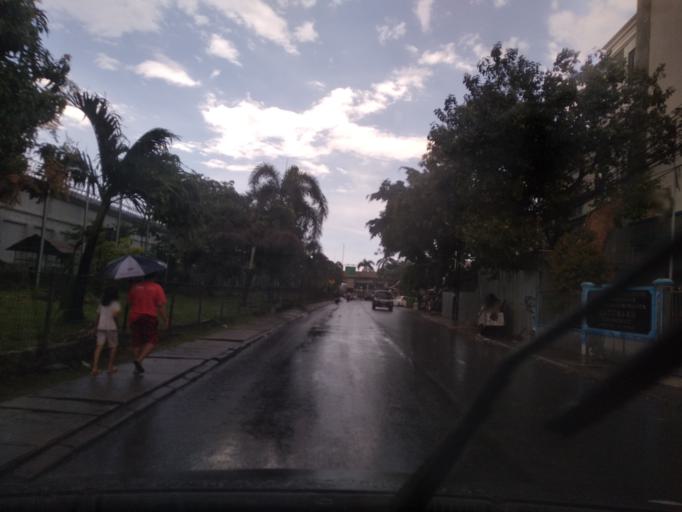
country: ID
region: Jakarta Raya
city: Jakarta
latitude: -6.2157
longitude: 106.8868
